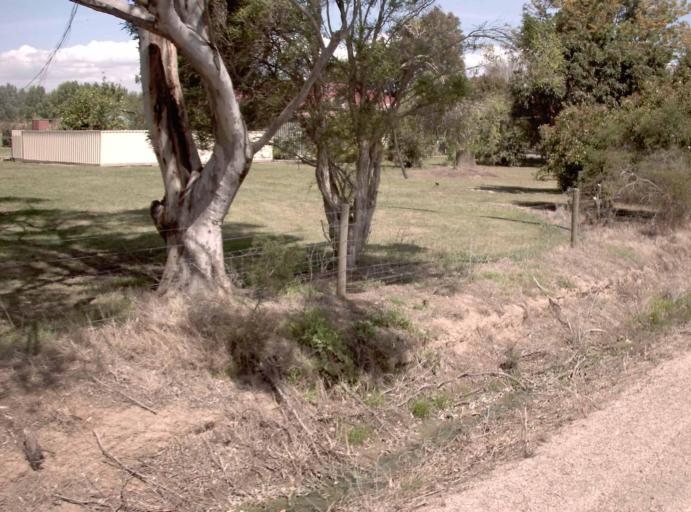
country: AU
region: Victoria
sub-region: Wellington
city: Heyfield
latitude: -38.0361
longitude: 146.8781
